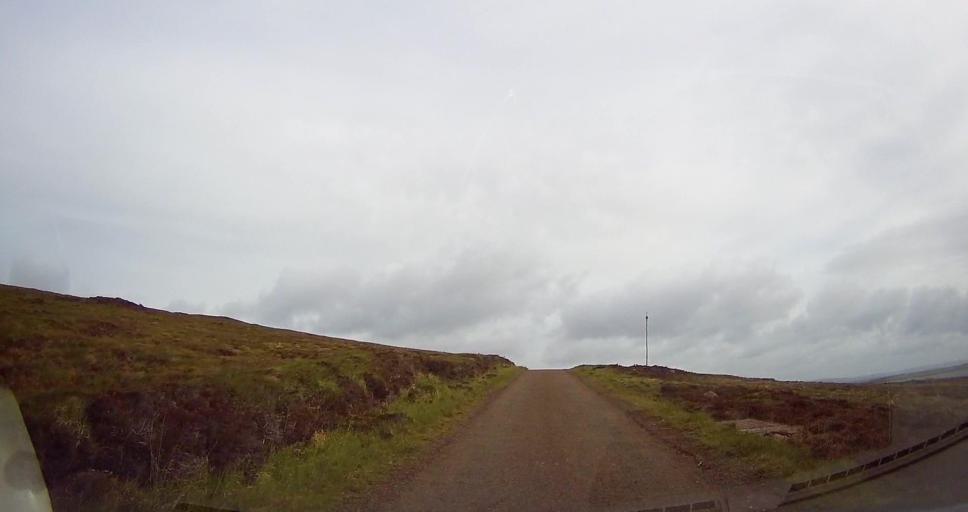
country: GB
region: Scotland
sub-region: Orkney Islands
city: Stromness
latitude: 58.8639
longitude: -3.2214
